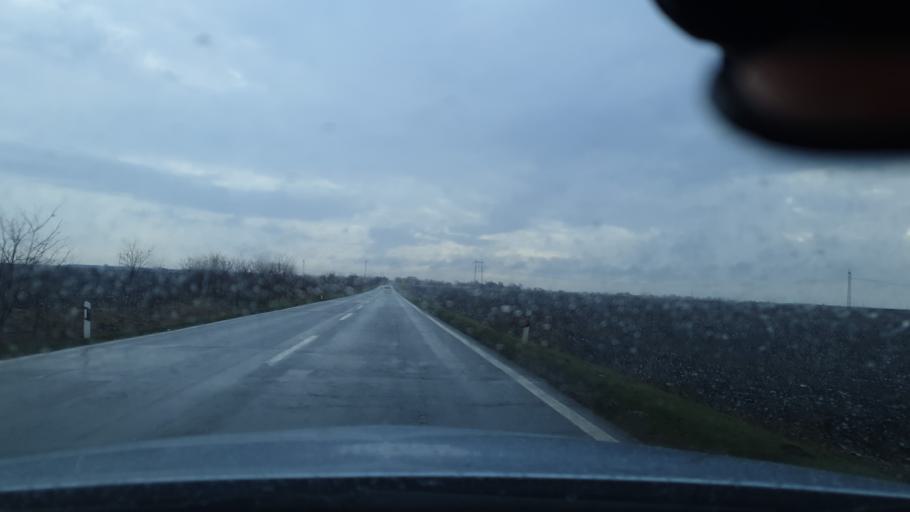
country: RS
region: Autonomna Pokrajina Vojvodina
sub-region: Juznobanatski Okrug
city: Kovin
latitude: 44.8280
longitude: 20.8415
